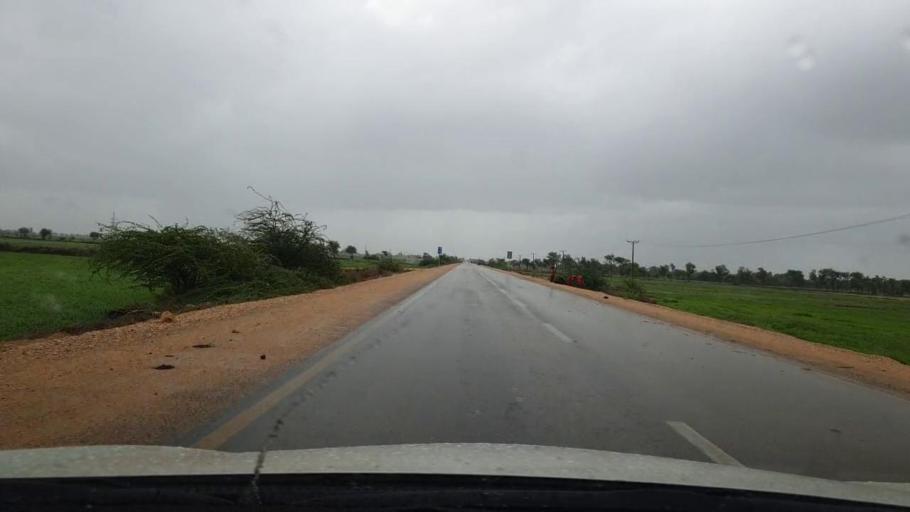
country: PK
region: Sindh
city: Kario
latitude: 24.6533
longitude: 68.5830
